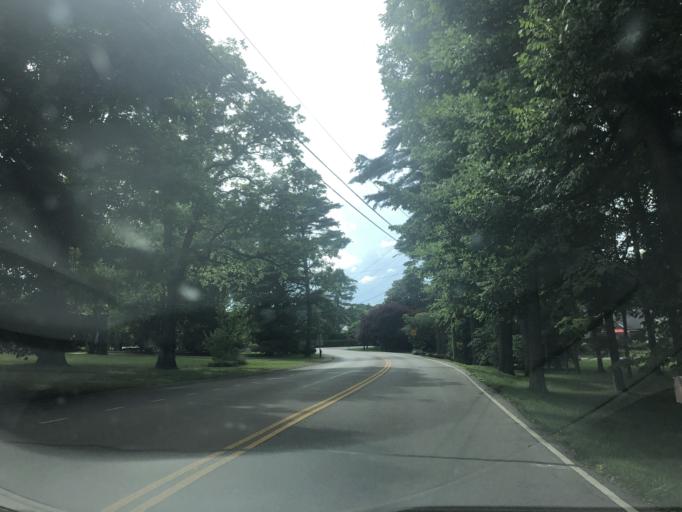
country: US
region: Tennessee
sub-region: Davidson County
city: Oak Hill
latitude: 36.0822
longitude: -86.7761
